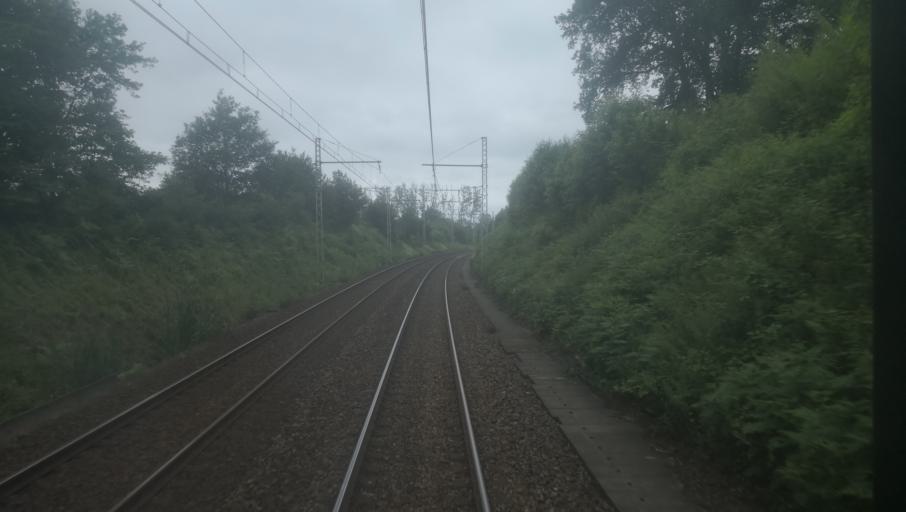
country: FR
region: Centre
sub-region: Departement de l'Indre
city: Chantome
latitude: 46.4338
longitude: 1.5545
